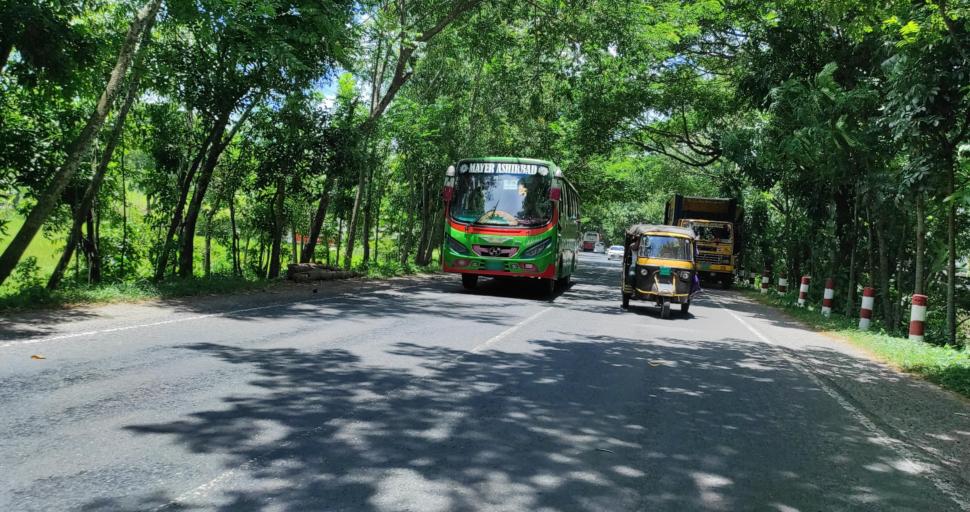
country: BD
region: Barisal
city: Gaurnadi
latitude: 22.8400
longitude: 90.2514
